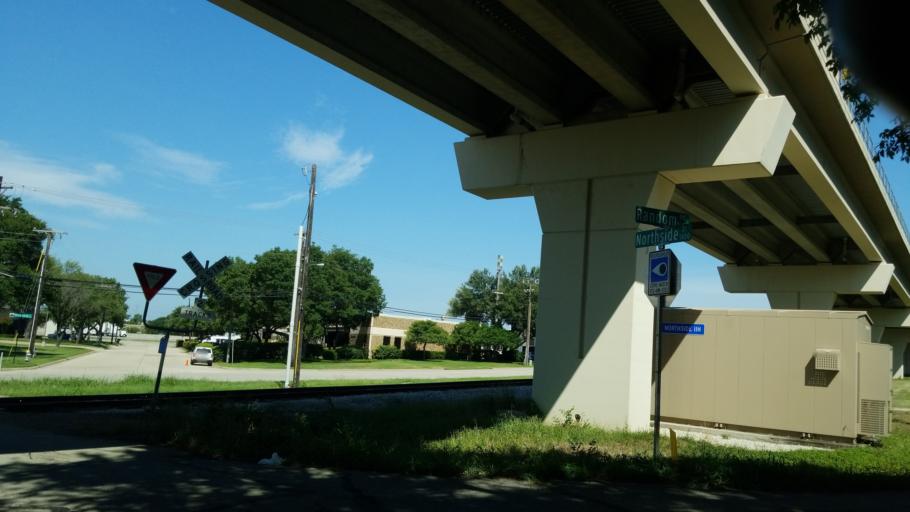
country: US
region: Texas
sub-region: Dallas County
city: Carrollton
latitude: 32.9599
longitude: -96.9120
